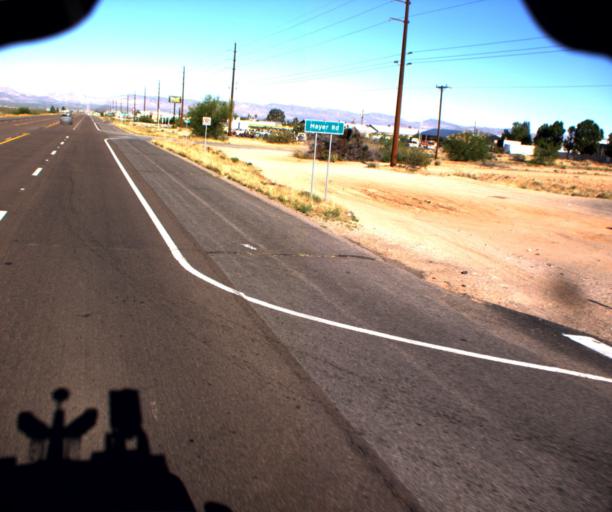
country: US
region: Arizona
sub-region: Mohave County
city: Golden Valley
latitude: 35.2216
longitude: -114.2057
